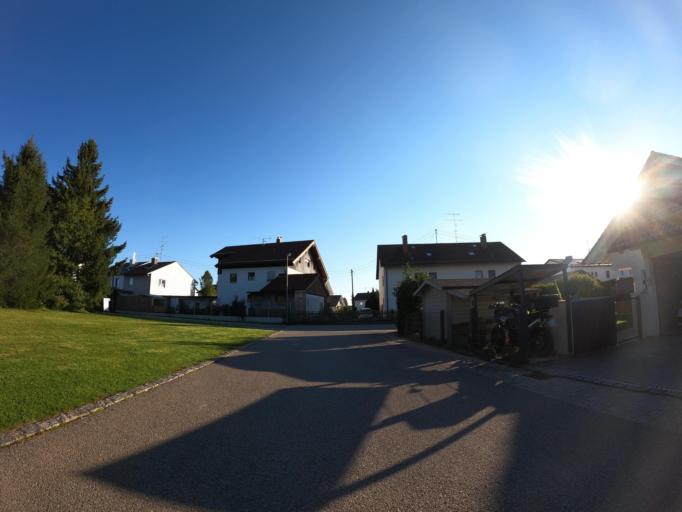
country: DE
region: Bavaria
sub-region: Upper Bavaria
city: Grasbrunn
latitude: 48.0591
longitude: 11.7765
